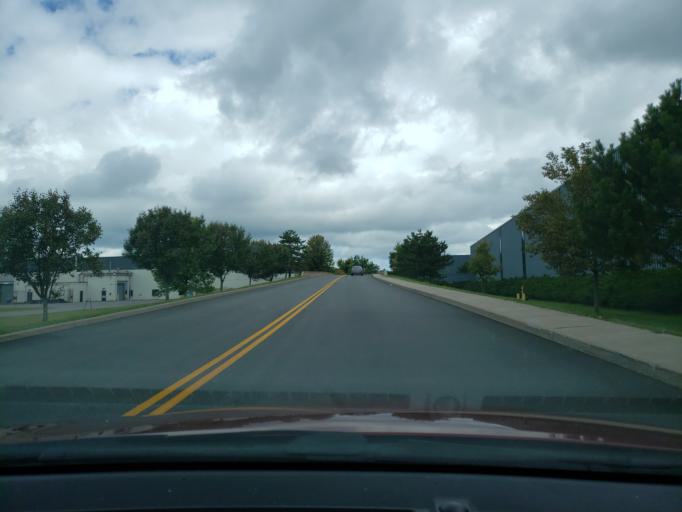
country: US
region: New York
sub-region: Monroe County
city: North Gates
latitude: 43.1510
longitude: -77.7407
